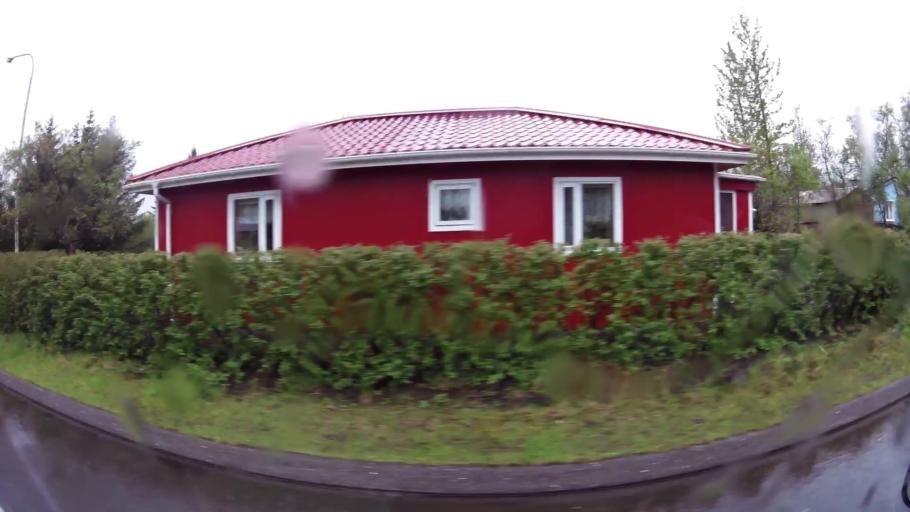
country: IS
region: South
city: Hveragerdi
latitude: 64.0035
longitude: -21.1929
